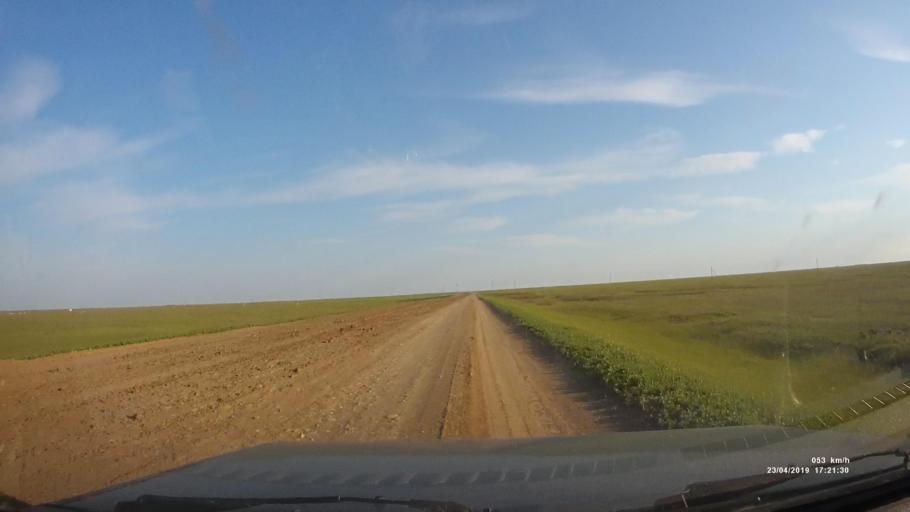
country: RU
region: Kalmykiya
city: Priyutnoye
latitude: 46.1757
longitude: 43.5054
